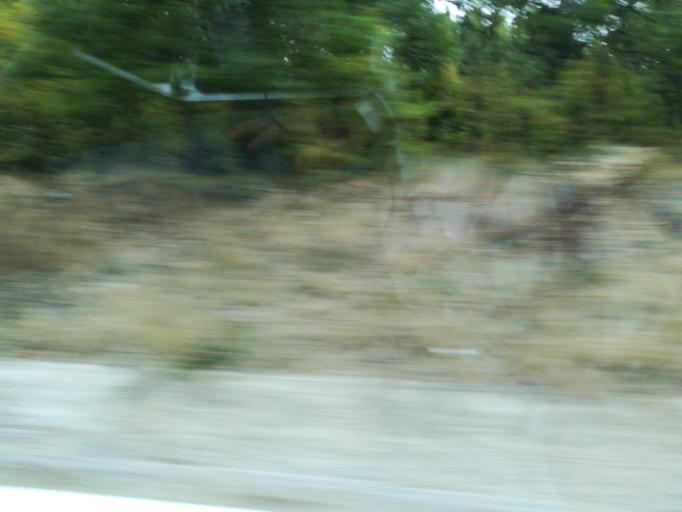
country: RO
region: Tulcea
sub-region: Comuna Horia
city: Horia
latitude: 44.9960
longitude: 28.4517
